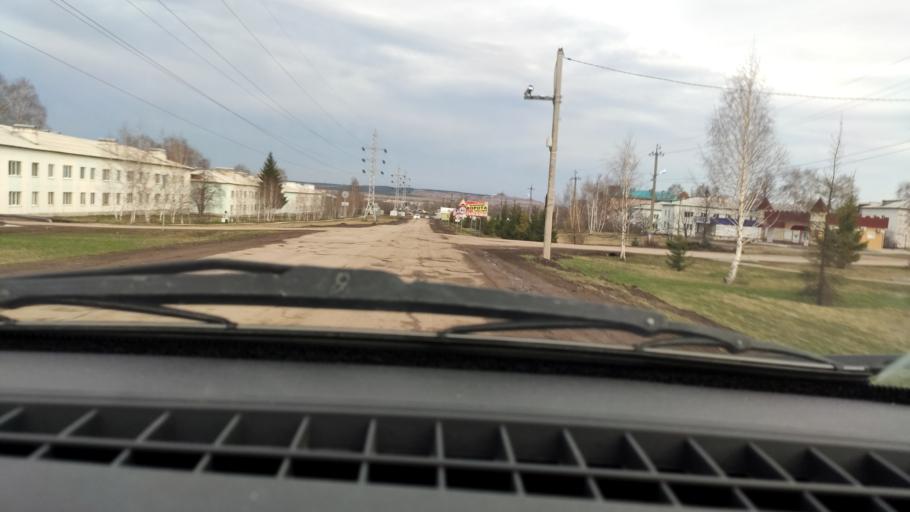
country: RU
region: Bashkortostan
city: Davlekanovo
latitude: 54.2251
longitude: 55.0381
